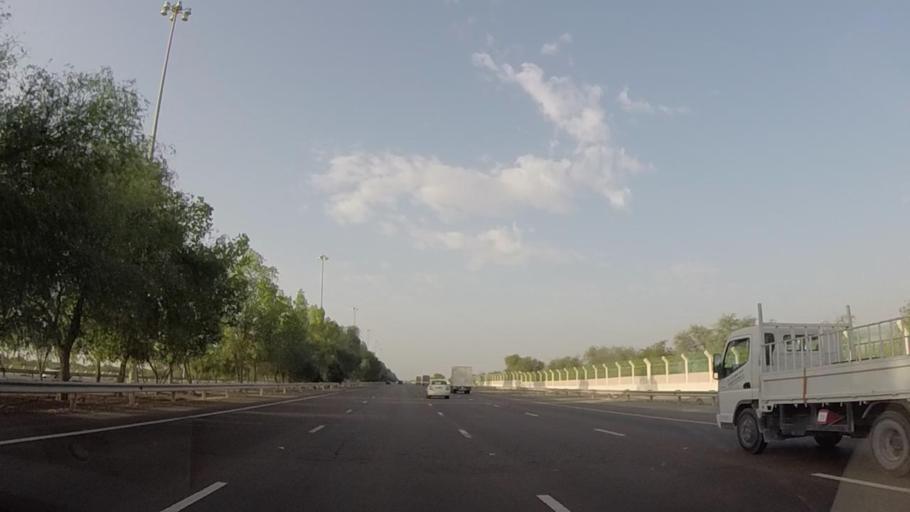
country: AE
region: Dubai
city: Dubai
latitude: 24.7228
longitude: 54.8091
